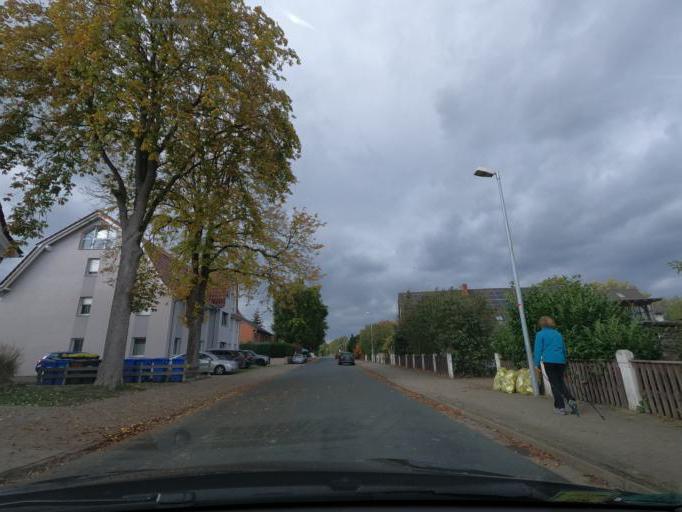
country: DE
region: Lower Saxony
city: Klein Schwulper
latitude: 52.3373
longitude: 10.4352
